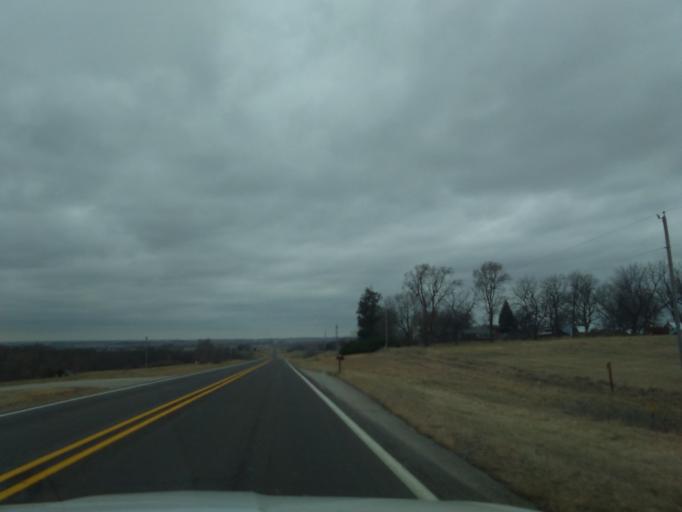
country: US
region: Nebraska
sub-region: Richardson County
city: Falls City
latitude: 40.0579
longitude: -95.4776
